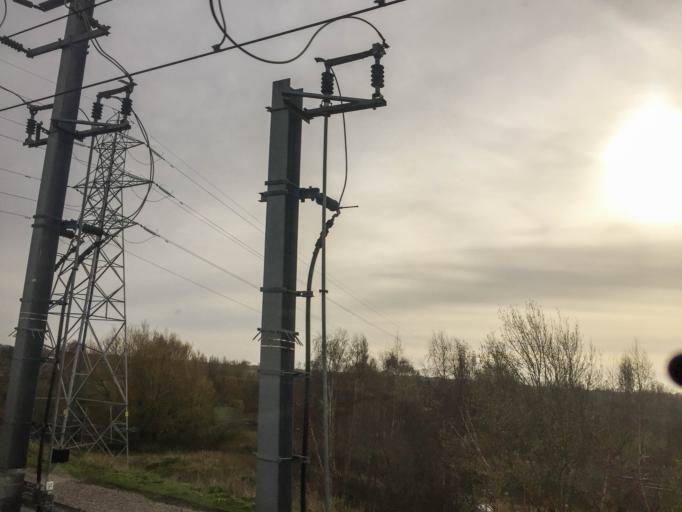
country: GB
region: England
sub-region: Warrington
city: Warrington
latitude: 53.3734
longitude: -2.6071
